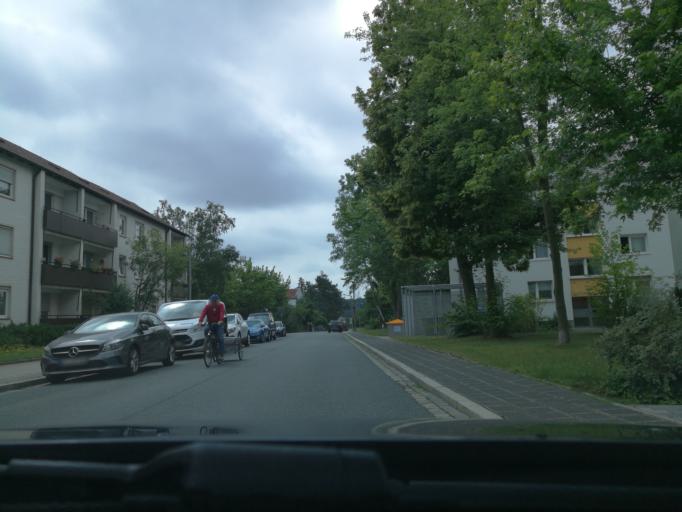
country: DE
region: Bavaria
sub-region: Regierungsbezirk Mittelfranken
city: Furth
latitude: 49.4776
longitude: 10.9706
